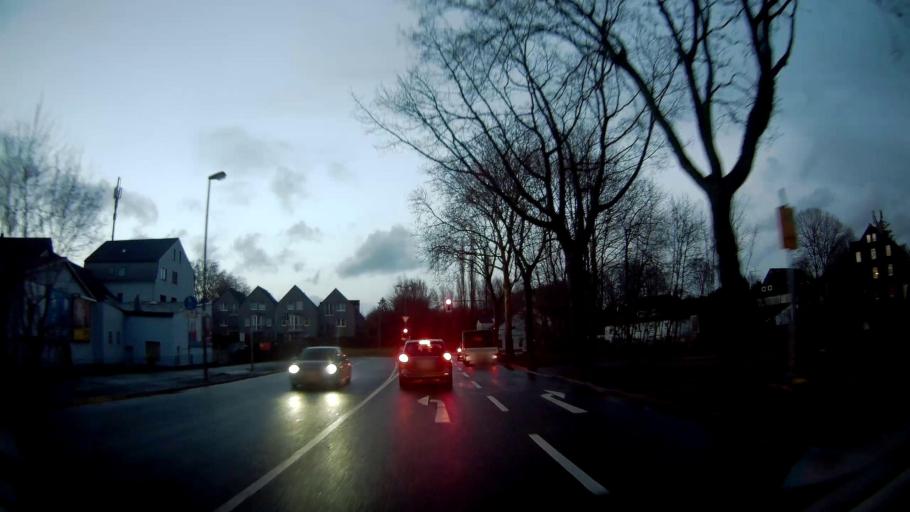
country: DE
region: North Rhine-Westphalia
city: Castrop-Rauxel
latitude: 51.5000
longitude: 7.2892
